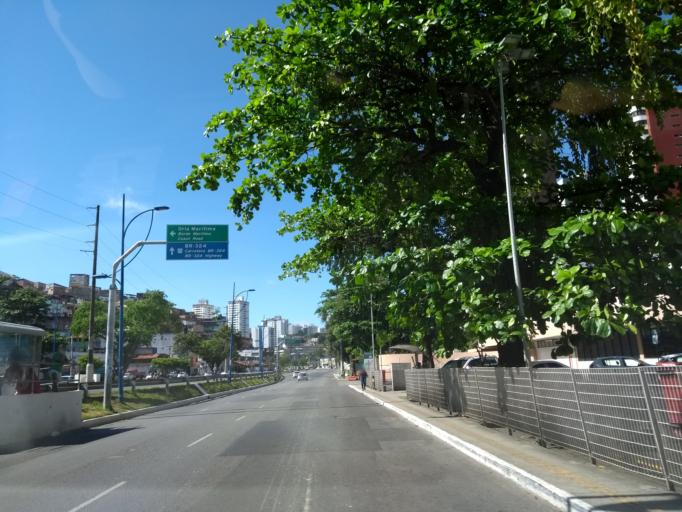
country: BR
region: Bahia
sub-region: Salvador
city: Salvador
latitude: -13.0024
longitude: -38.4920
